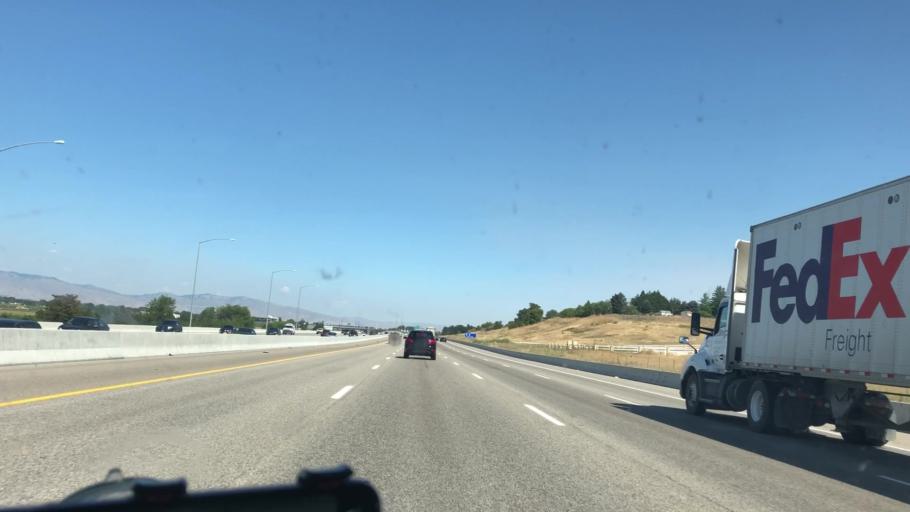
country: US
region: Idaho
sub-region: Ada County
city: Meridian
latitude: 43.5945
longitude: -116.4517
